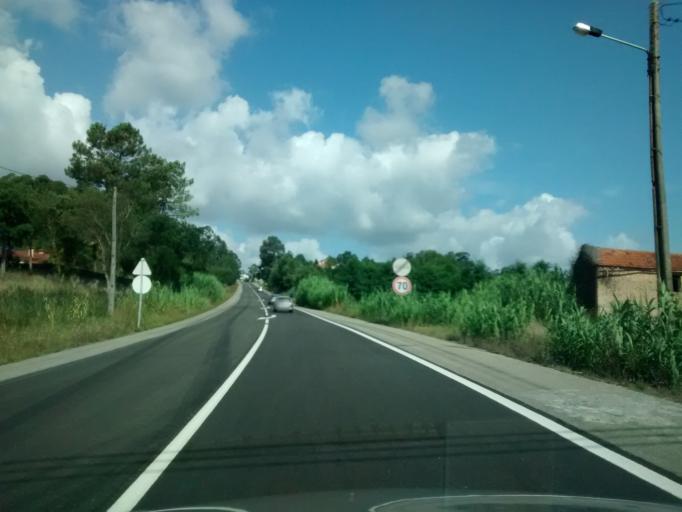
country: PT
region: Aveiro
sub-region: Oliveira do Bairro
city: Oliveira do Bairro
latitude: 40.5342
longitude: -8.5107
